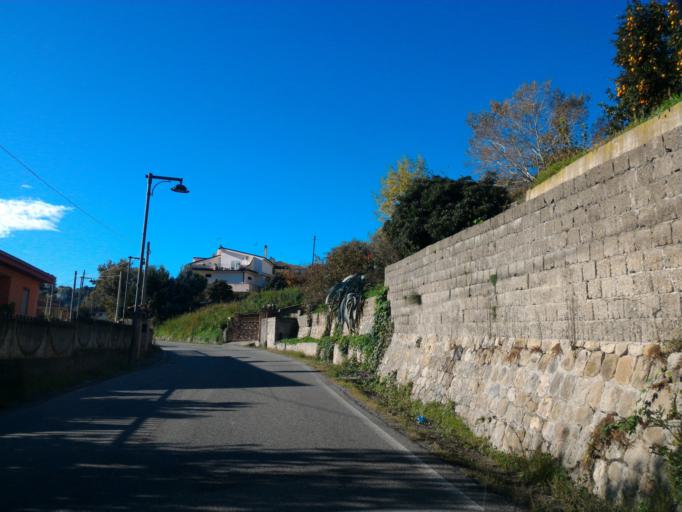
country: IT
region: Calabria
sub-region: Provincia di Crotone
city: Torretta
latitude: 39.4454
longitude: 17.0386
